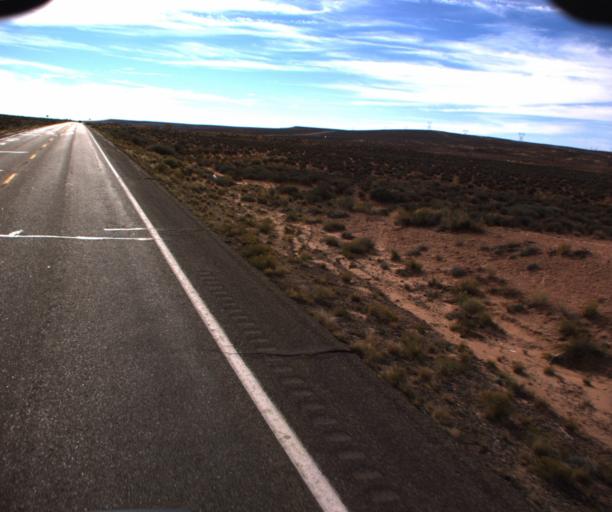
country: US
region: Arizona
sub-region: Coconino County
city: LeChee
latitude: 36.8314
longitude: -111.3143
